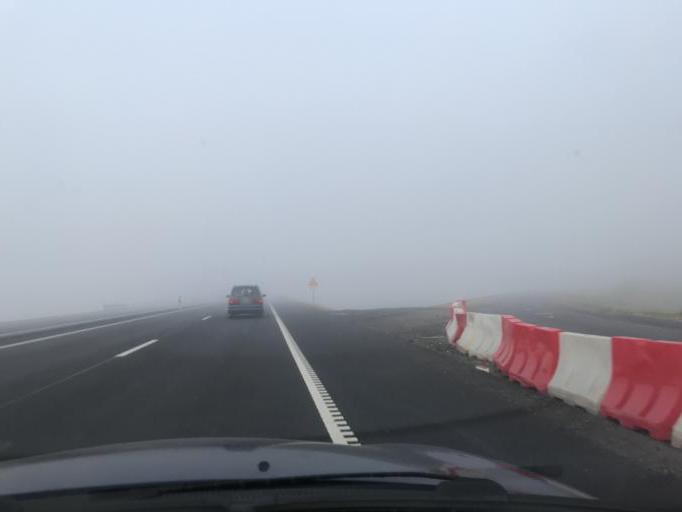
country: BY
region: Minsk
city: Valozhyn
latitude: 54.0404
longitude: 26.6729
